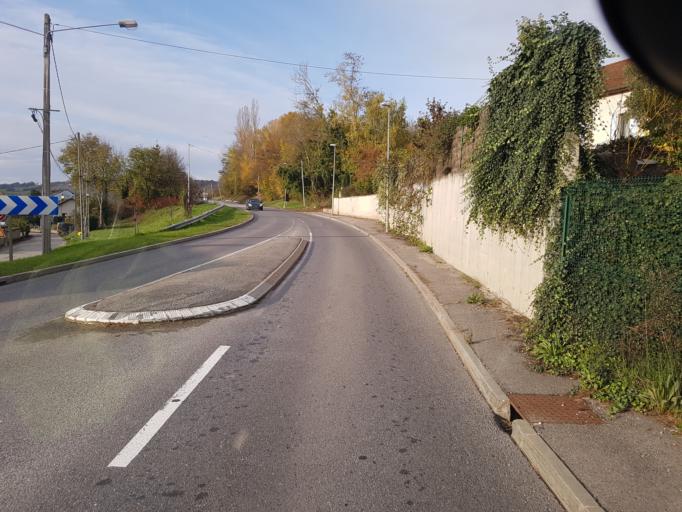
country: FR
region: Rhone-Alpes
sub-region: Departement de la Haute-Savoie
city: Frangy
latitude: 46.0432
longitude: 5.8857
